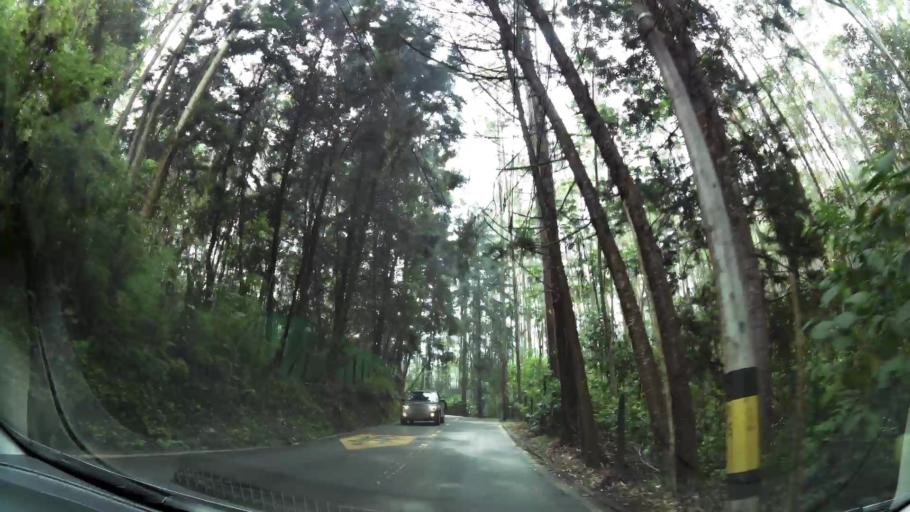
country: CO
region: Antioquia
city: Medellin
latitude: 6.2046
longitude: -75.5488
